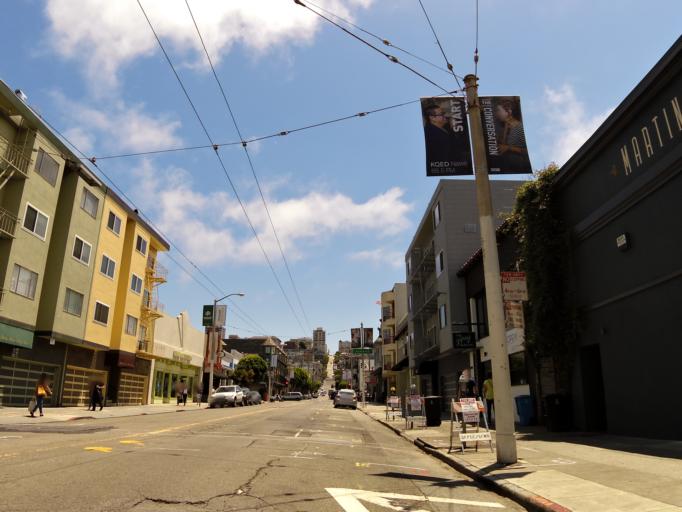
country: US
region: California
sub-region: San Francisco County
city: San Francisco
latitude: 37.8007
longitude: -122.4363
